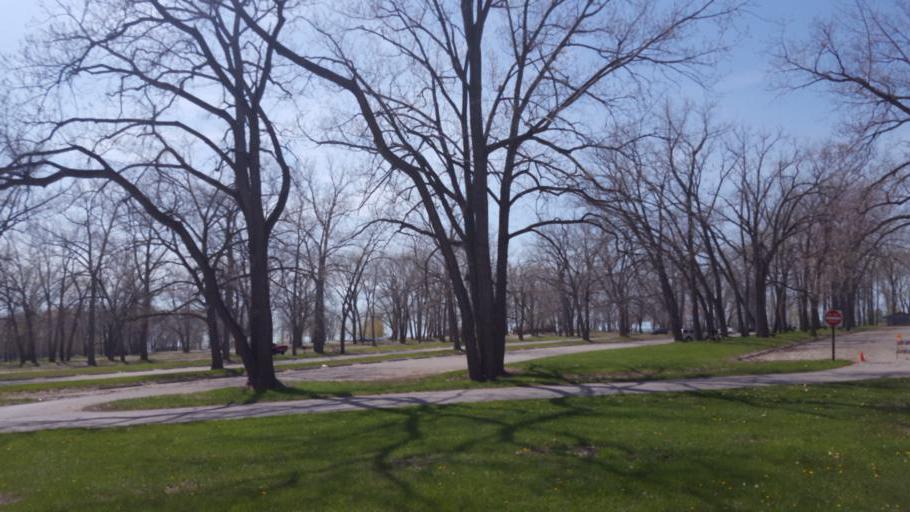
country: US
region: Ohio
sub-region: Lake County
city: Fairport Harbor
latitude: 41.7575
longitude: -81.2837
